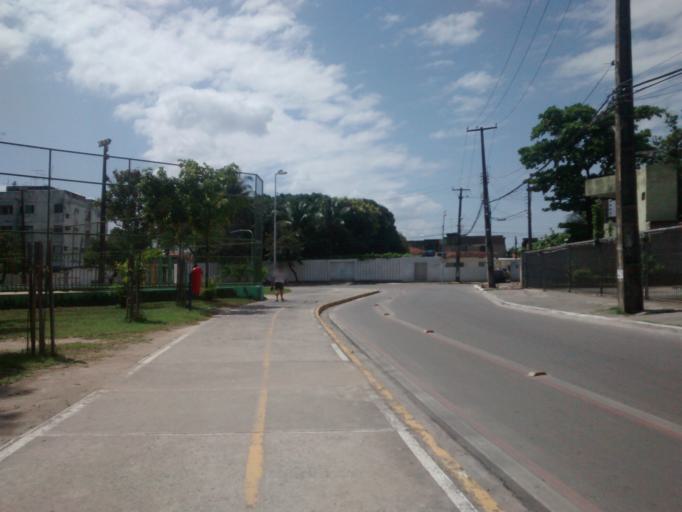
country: BR
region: Pernambuco
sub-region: Recife
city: Recife
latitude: -8.0929
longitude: -34.9132
